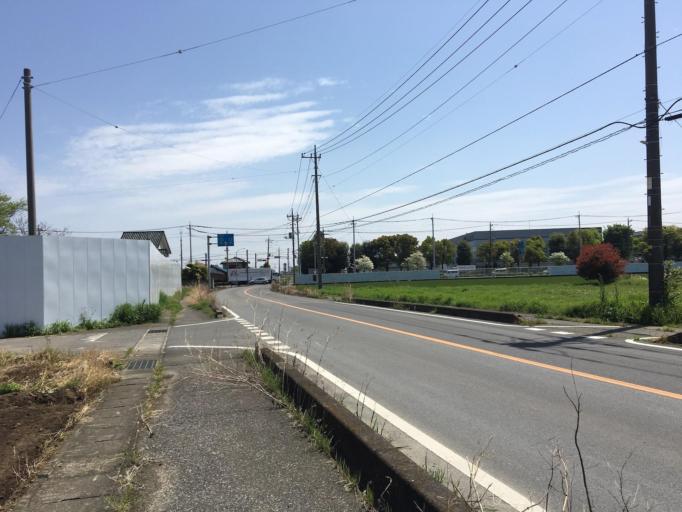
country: JP
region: Gunma
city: Sakai-nakajima
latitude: 36.2791
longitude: 139.2806
